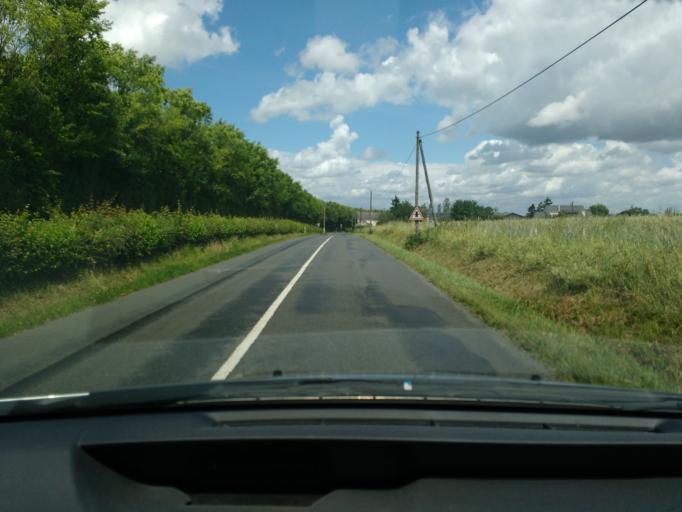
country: FR
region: Pays de la Loire
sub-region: Departement de Maine-et-Loire
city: Trelaze
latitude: 47.4761
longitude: -0.4914
